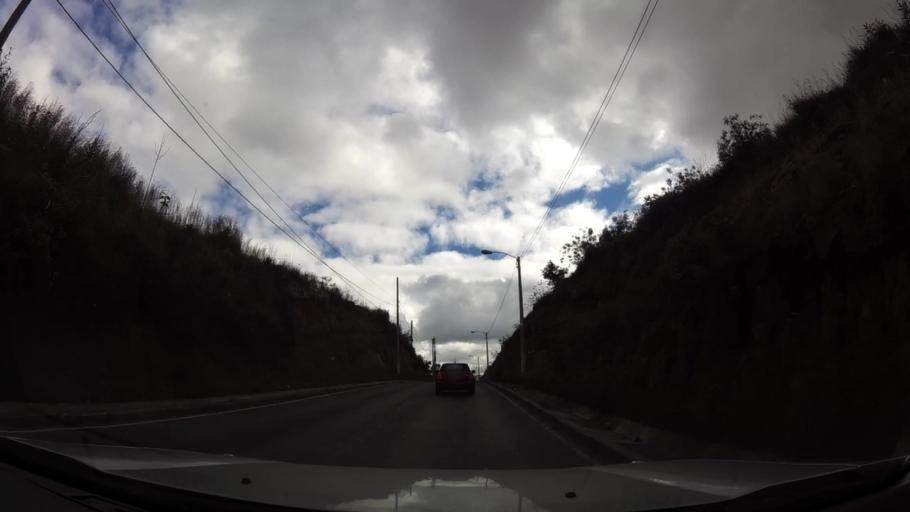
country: GT
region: Guatemala
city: Guatemala City
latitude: 14.6688
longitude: -90.5542
